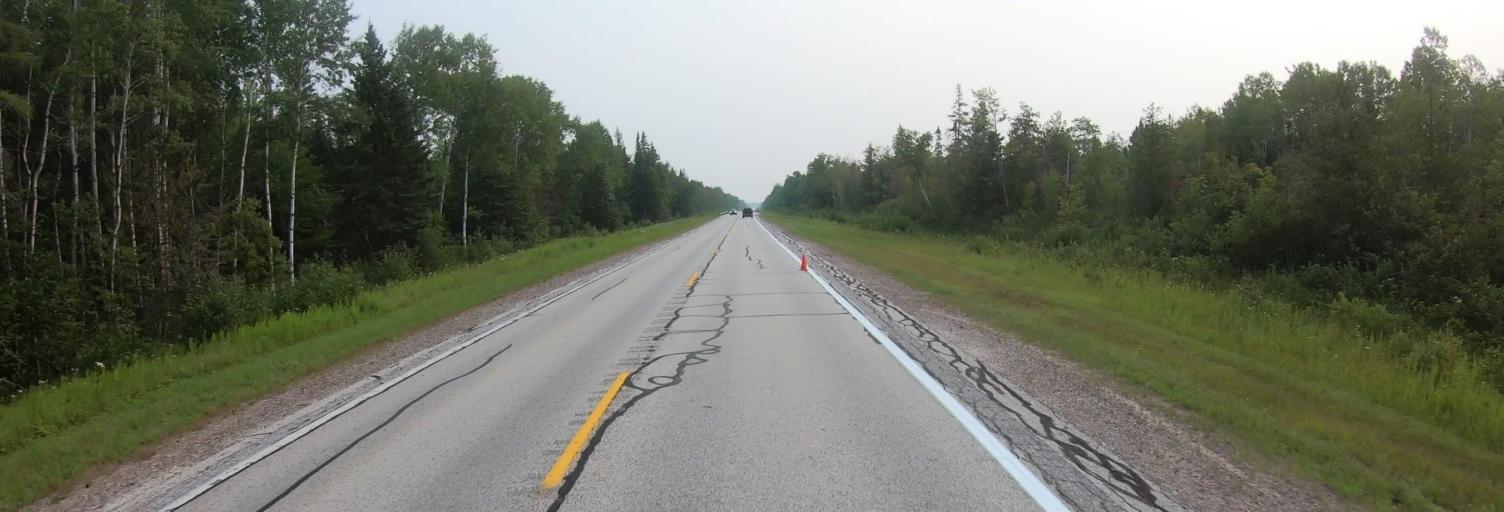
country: US
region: Michigan
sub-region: Luce County
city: Newberry
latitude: 46.5191
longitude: -85.0788
